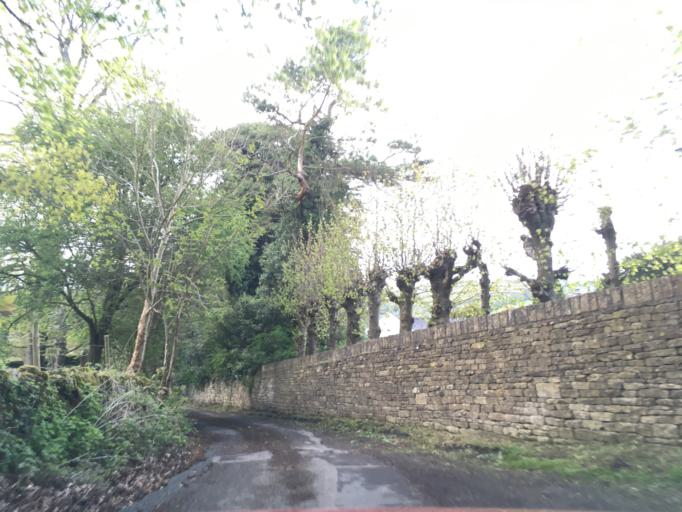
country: GB
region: England
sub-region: Gloucestershire
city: Brimscombe
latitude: 51.7150
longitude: -2.1948
